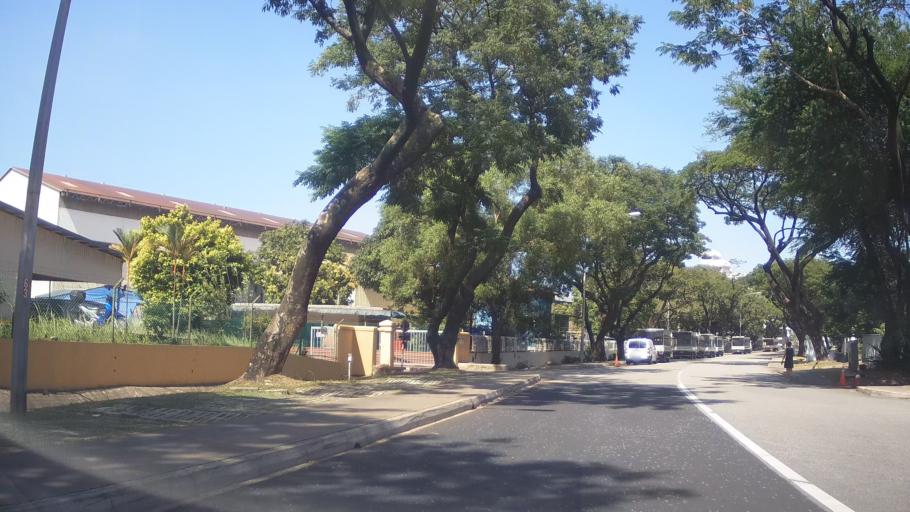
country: SG
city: Singapore
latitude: 1.3049
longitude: 103.7032
